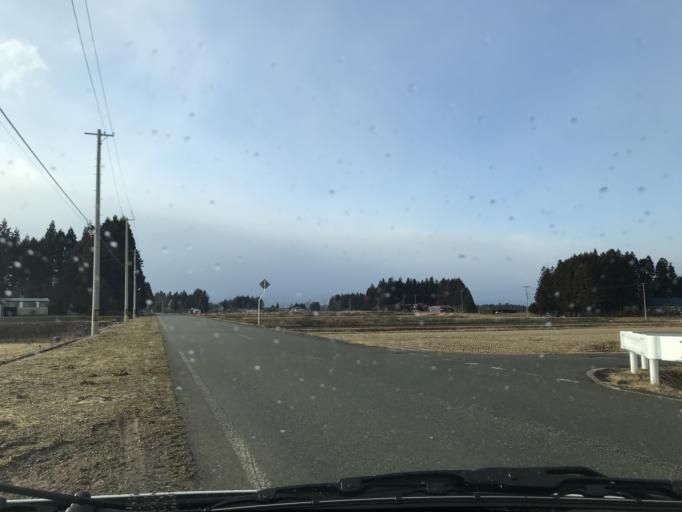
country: JP
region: Iwate
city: Mizusawa
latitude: 39.0926
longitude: 141.0304
